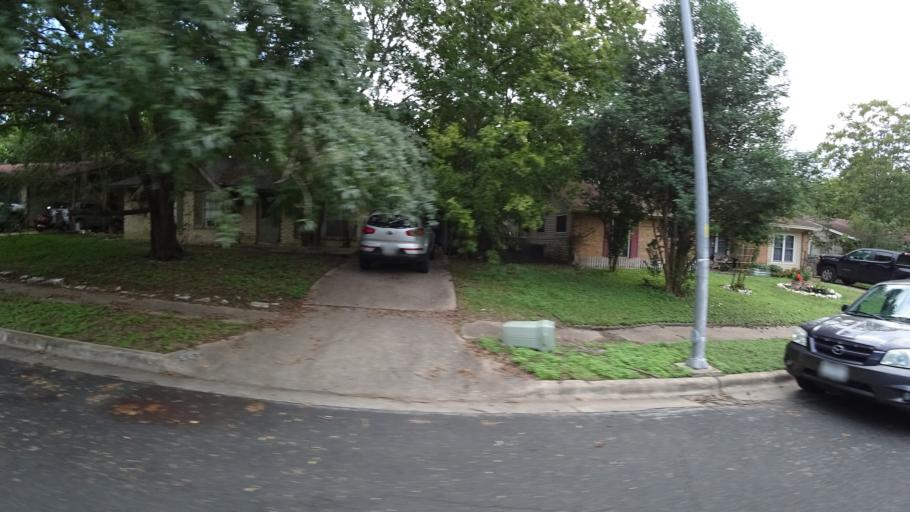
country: US
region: Texas
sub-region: Travis County
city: Onion Creek
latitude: 30.2025
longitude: -97.7826
